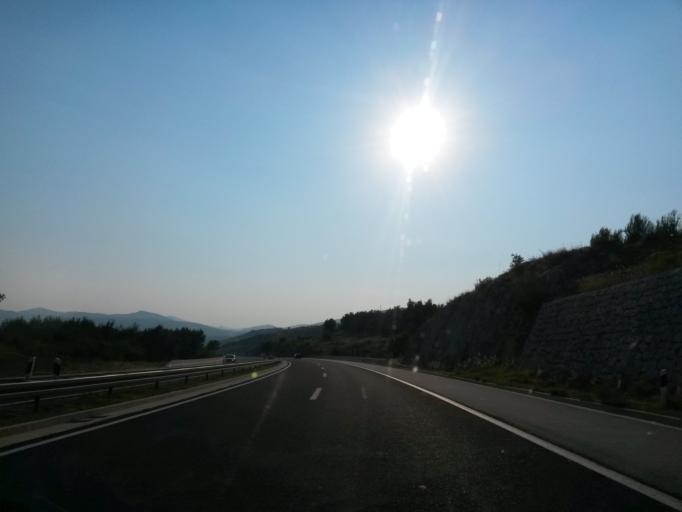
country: HR
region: Splitsko-Dalmatinska
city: Dugopolje
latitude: 43.6033
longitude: 16.6167
